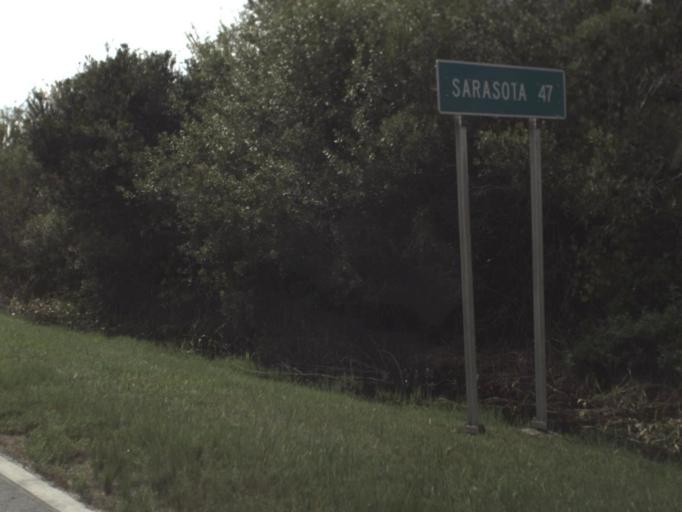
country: US
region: Florida
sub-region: DeSoto County
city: Arcadia
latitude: 27.2249
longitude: -81.8894
